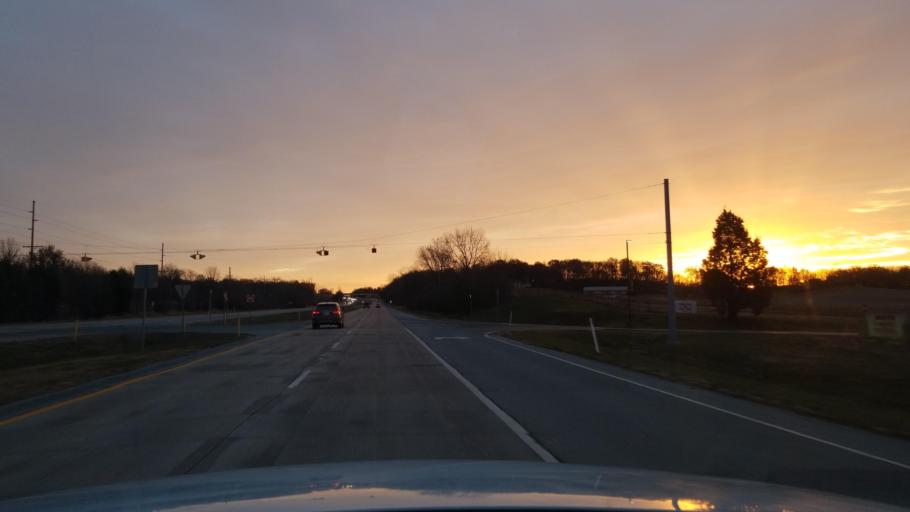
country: US
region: Indiana
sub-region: Posey County
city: Mount Vernon
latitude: 37.9418
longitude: -87.7512
